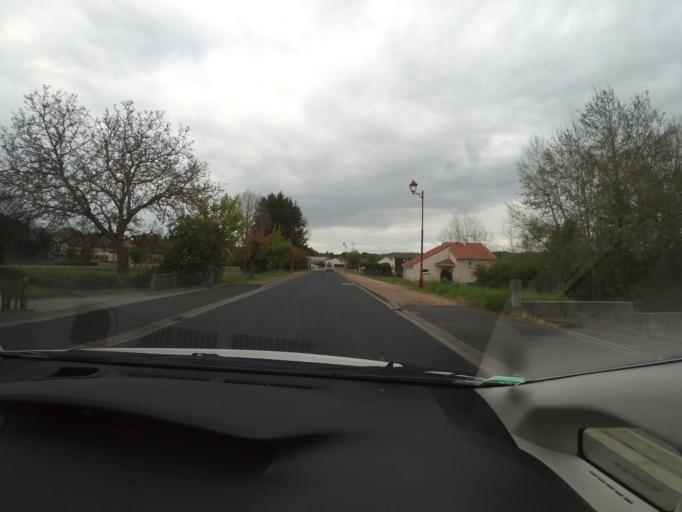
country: FR
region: Auvergne
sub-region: Departement du Puy-de-Dome
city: Gelles
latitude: 45.8423
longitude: 2.7612
